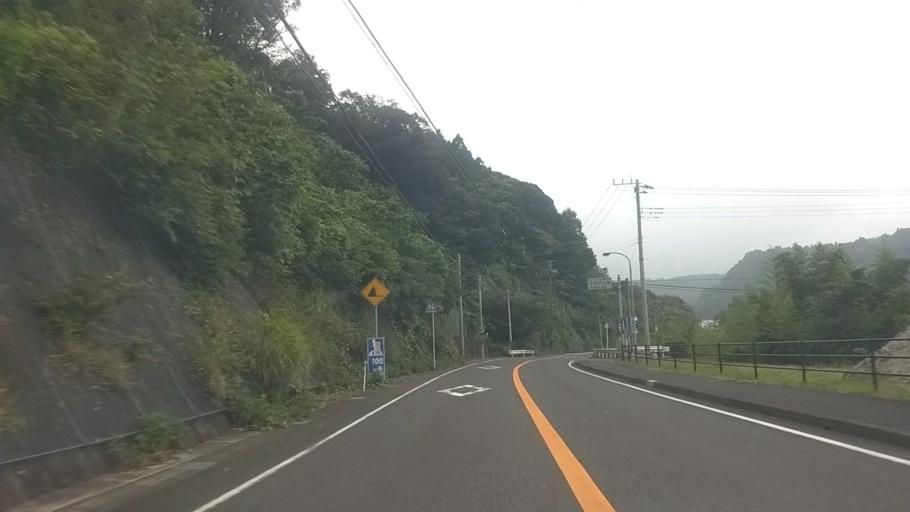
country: JP
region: Chiba
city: Katsuura
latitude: 35.2445
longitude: 140.2372
